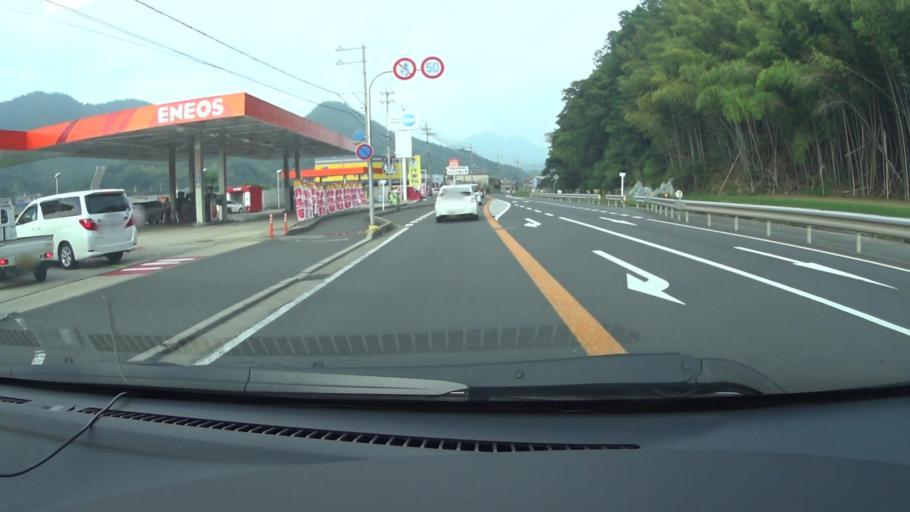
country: JP
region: Kyoto
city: Maizuru
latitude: 35.4800
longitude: 135.4142
